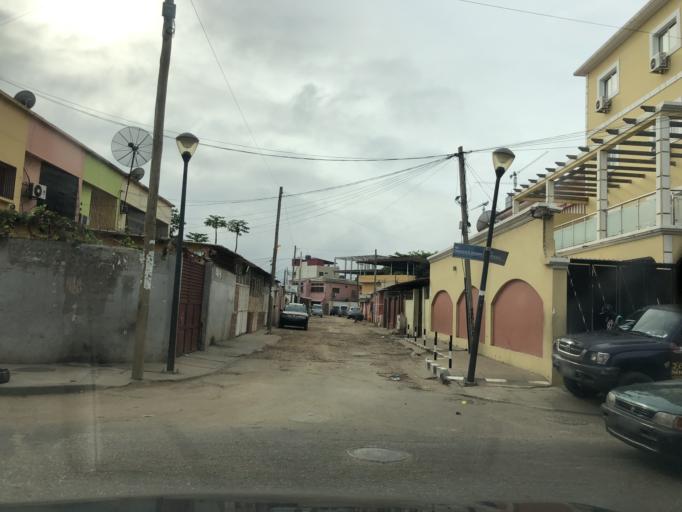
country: AO
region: Luanda
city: Luanda
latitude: -8.8218
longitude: 13.2518
